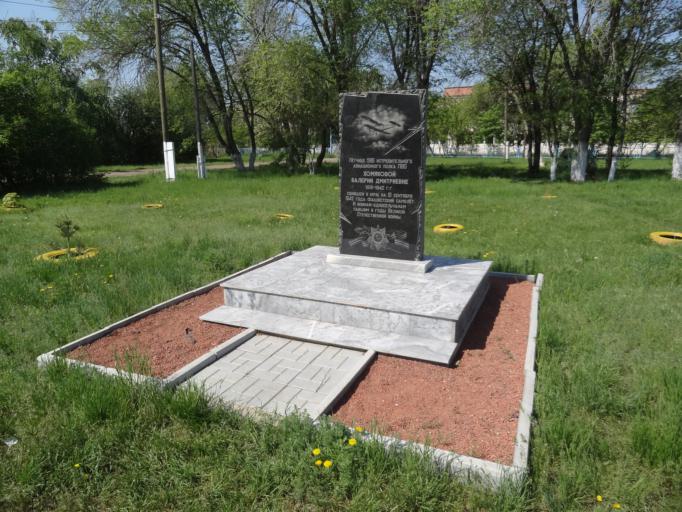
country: RU
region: Saratov
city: Privolzhskiy
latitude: 51.4106
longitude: 46.0973
